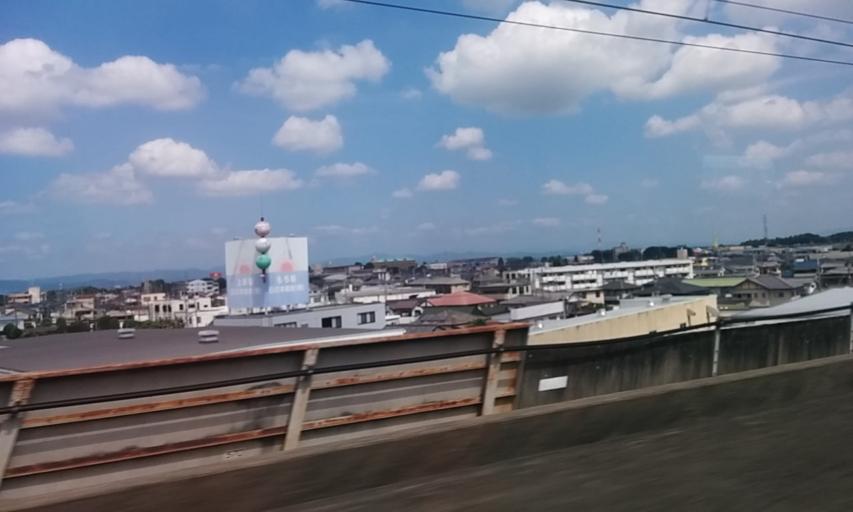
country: JP
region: Tochigi
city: Oyama
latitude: 36.3237
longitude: 139.8123
